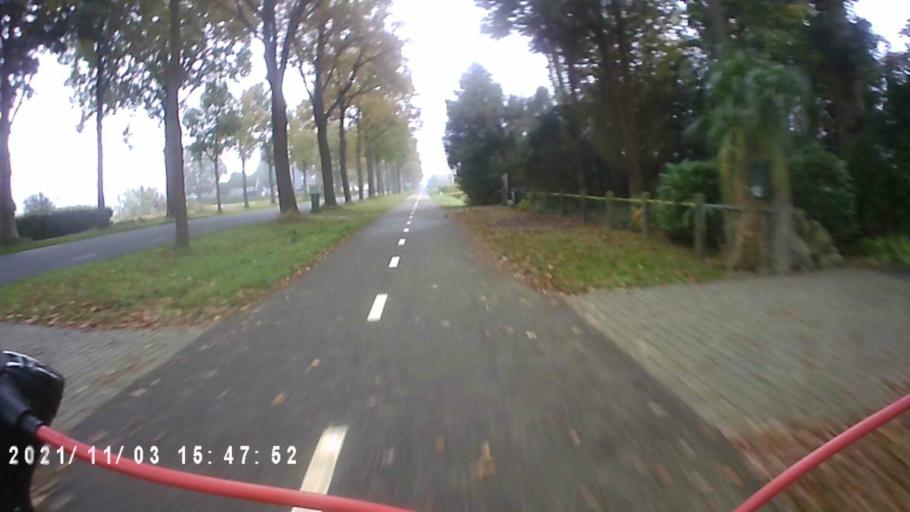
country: NL
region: Groningen
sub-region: Gemeente Leek
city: Leek
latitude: 53.0893
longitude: 6.3396
